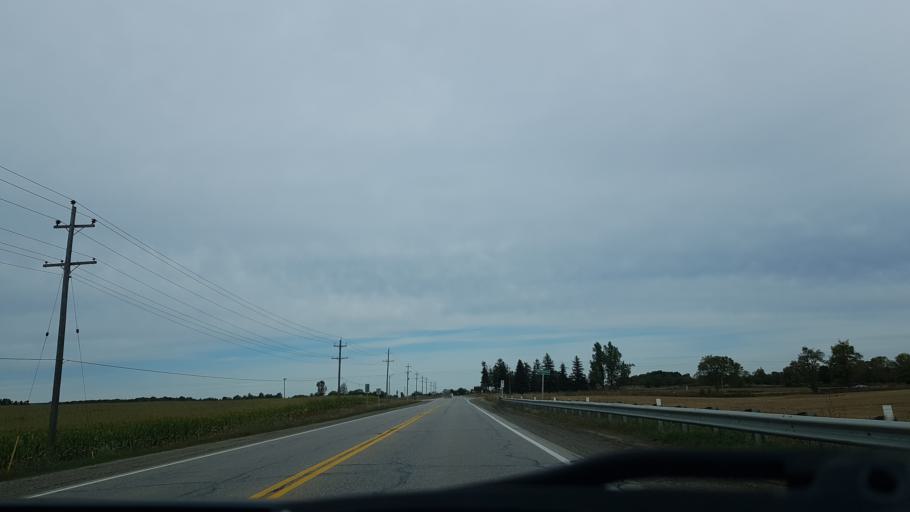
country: CA
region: Ontario
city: Orangeville
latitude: 43.8191
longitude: -80.0412
